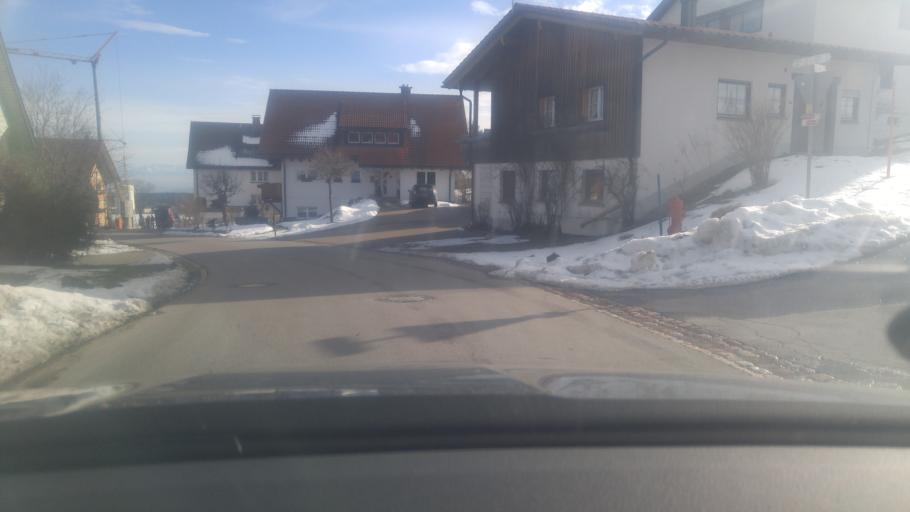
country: DE
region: Baden-Wuerttemberg
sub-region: Freiburg Region
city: Hochenschwand
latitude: 47.7176
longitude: 8.1514
